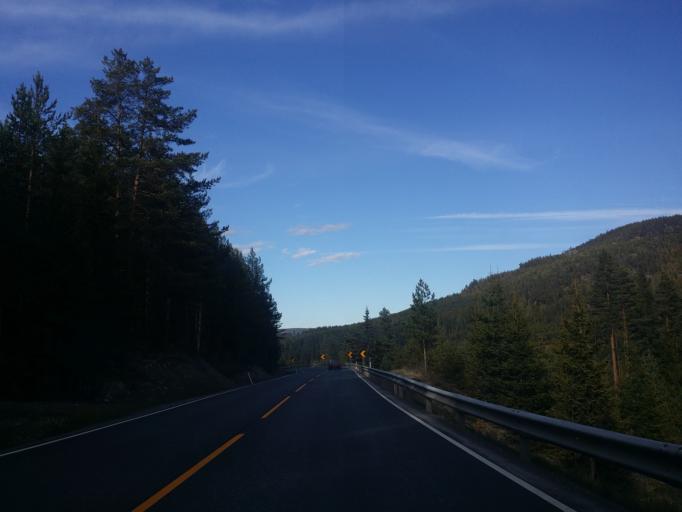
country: NO
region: Buskerud
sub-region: Kongsberg
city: Kongsberg
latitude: 59.6185
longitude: 9.4716
